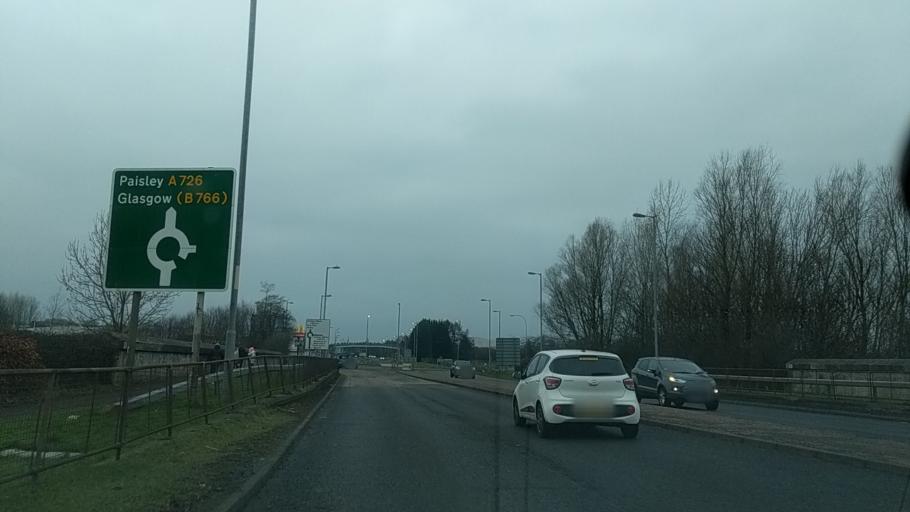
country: GB
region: Scotland
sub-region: South Lanarkshire
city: East Kilbride
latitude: 55.7645
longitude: -4.2075
